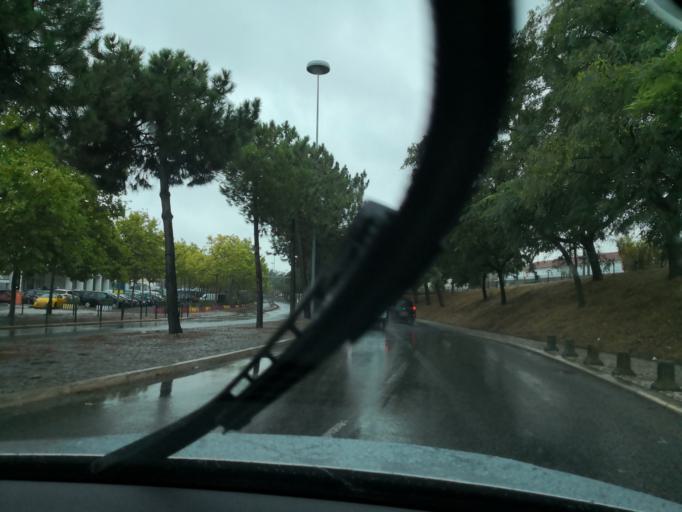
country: PT
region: Lisbon
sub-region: Loures
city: Moscavide
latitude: 38.7854
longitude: -9.1002
